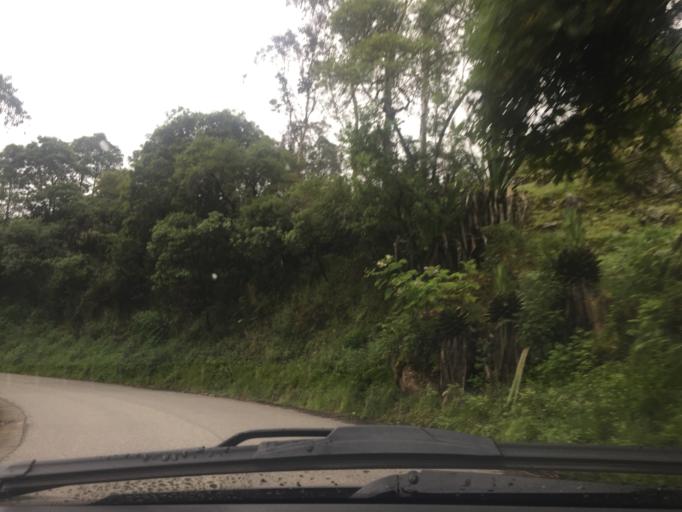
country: CO
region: Cundinamarca
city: Junin
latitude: 4.8132
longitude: -73.7325
